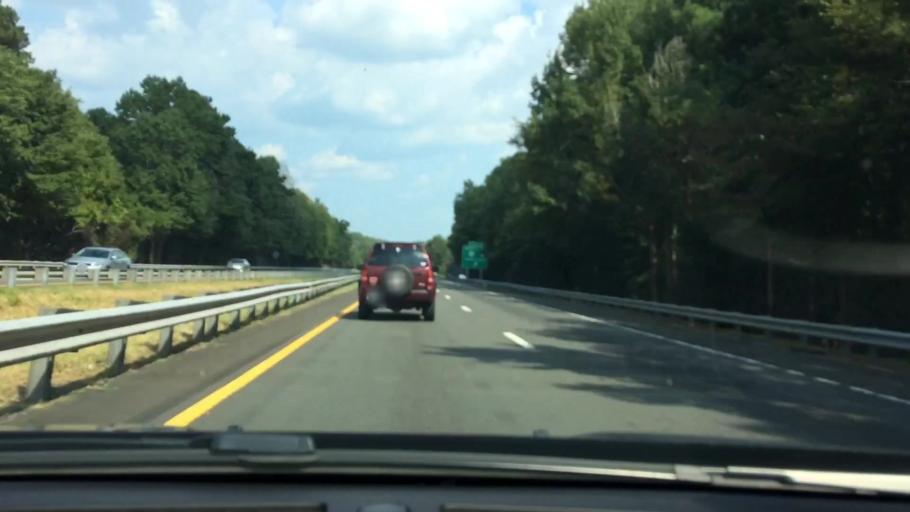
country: US
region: North Carolina
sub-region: Orange County
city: Hillsborough
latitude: 36.0387
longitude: -79.0163
